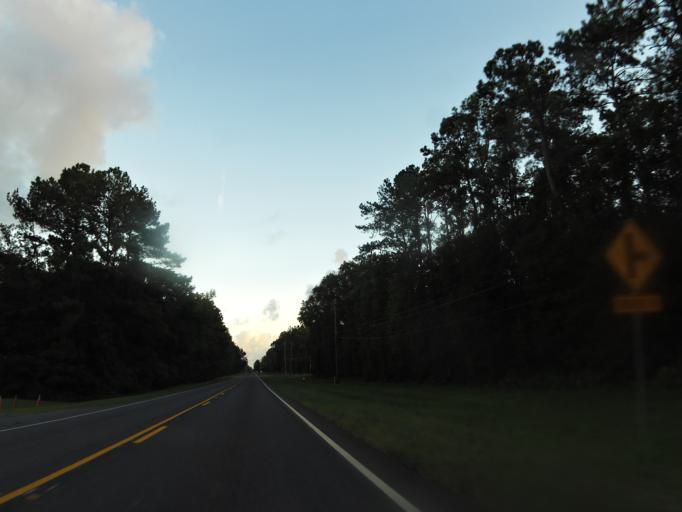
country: US
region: Georgia
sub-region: Camden County
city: Woodbine
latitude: 30.9225
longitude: -81.7142
